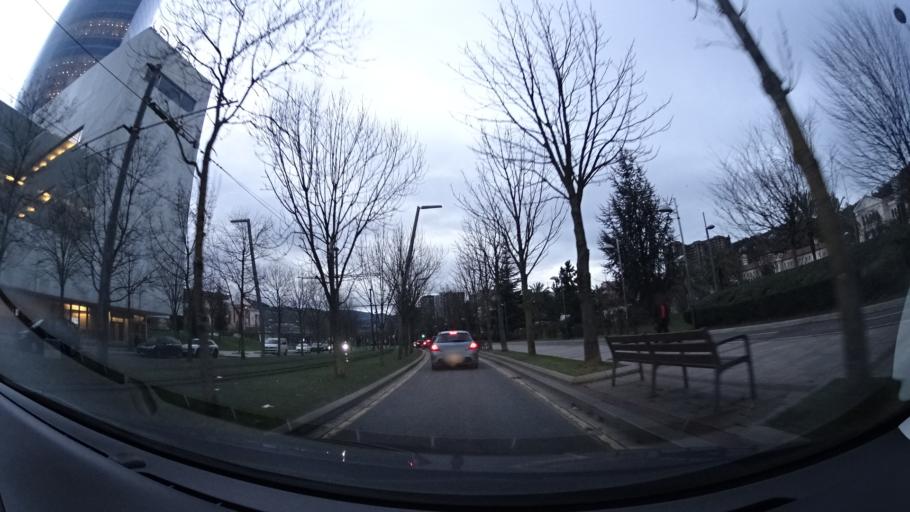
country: ES
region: Basque Country
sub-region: Bizkaia
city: Bilbao
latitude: 43.2690
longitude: -2.9376
